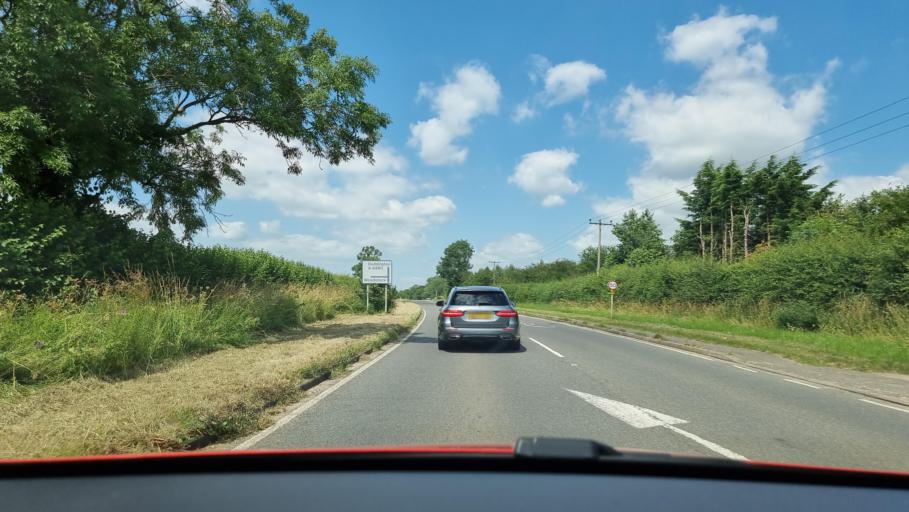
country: GB
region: England
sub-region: Oxfordshire
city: Kidlington
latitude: 51.8407
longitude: -1.3089
